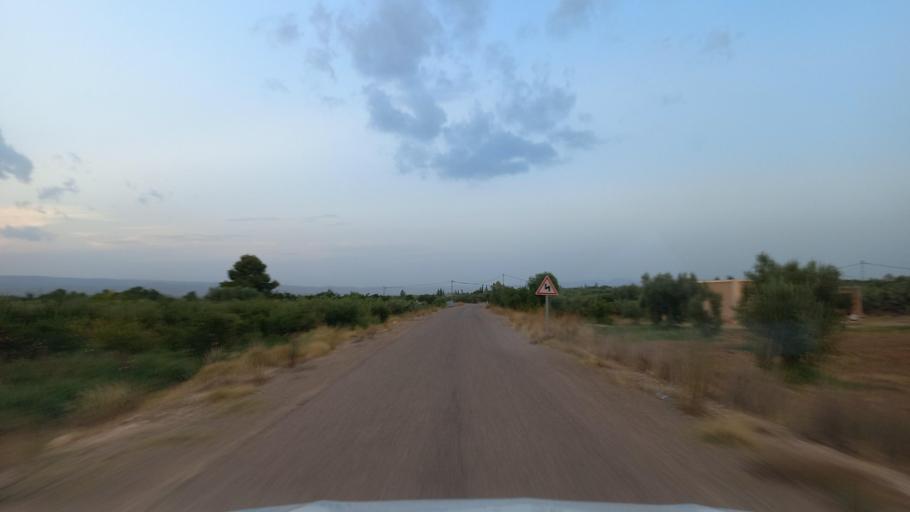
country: TN
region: Al Qasrayn
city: Kasserine
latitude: 35.2669
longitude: 9.0491
